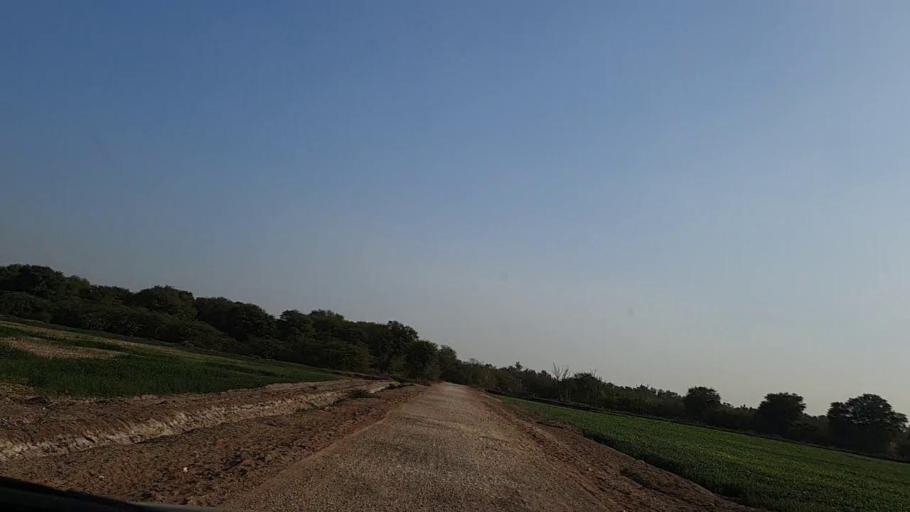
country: PK
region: Sindh
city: Sakrand
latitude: 26.0956
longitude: 68.2139
